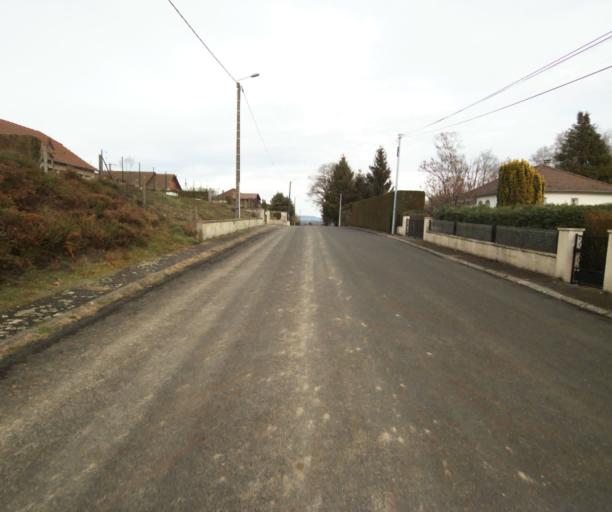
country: FR
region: Limousin
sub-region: Departement de la Correze
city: Saint-Mexant
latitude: 45.2681
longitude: 1.6828
